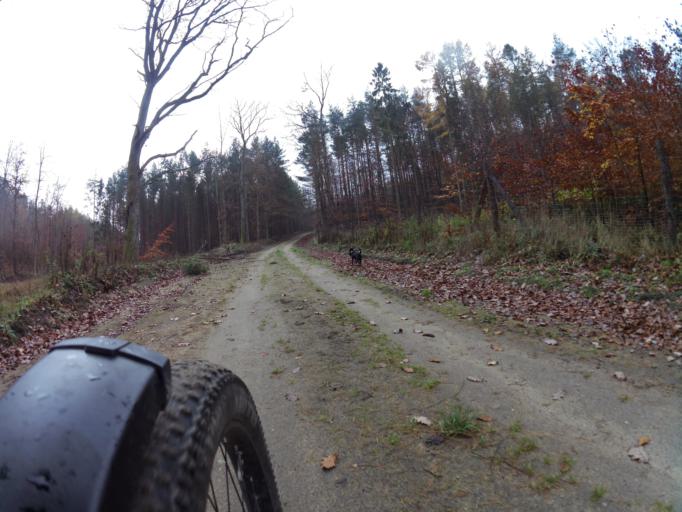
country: PL
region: Pomeranian Voivodeship
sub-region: Powiat pucki
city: Krokowa
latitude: 54.7785
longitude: 18.0919
